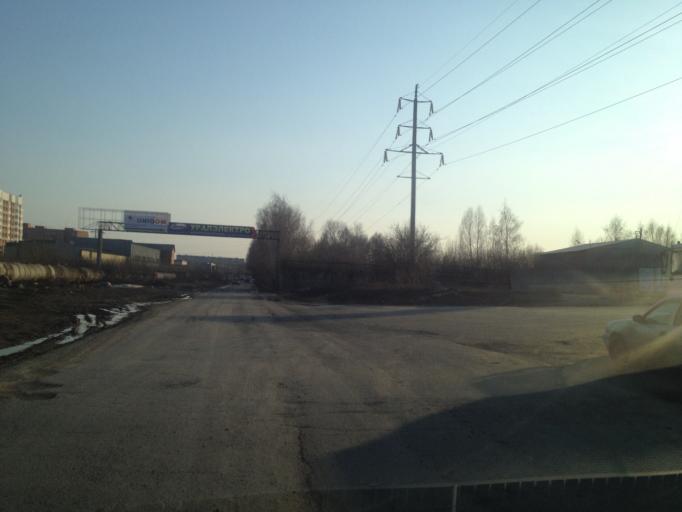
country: RU
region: Sverdlovsk
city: Yekaterinburg
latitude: 56.8767
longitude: 60.5452
